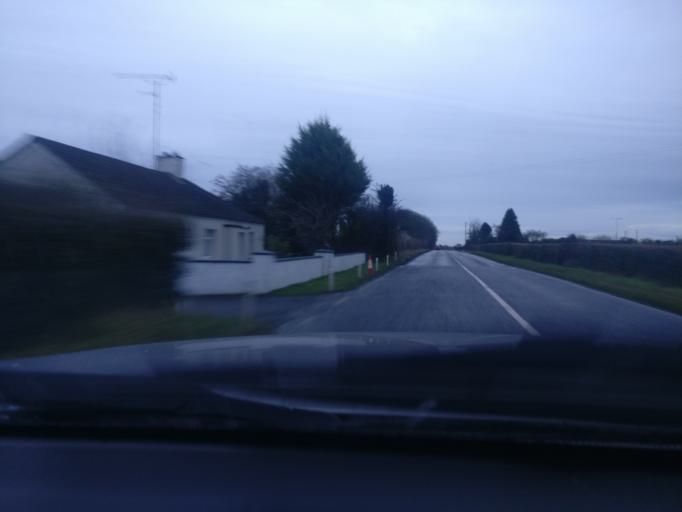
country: IE
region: Leinster
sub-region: An Mhi
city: Navan
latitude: 53.6828
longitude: -6.7610
